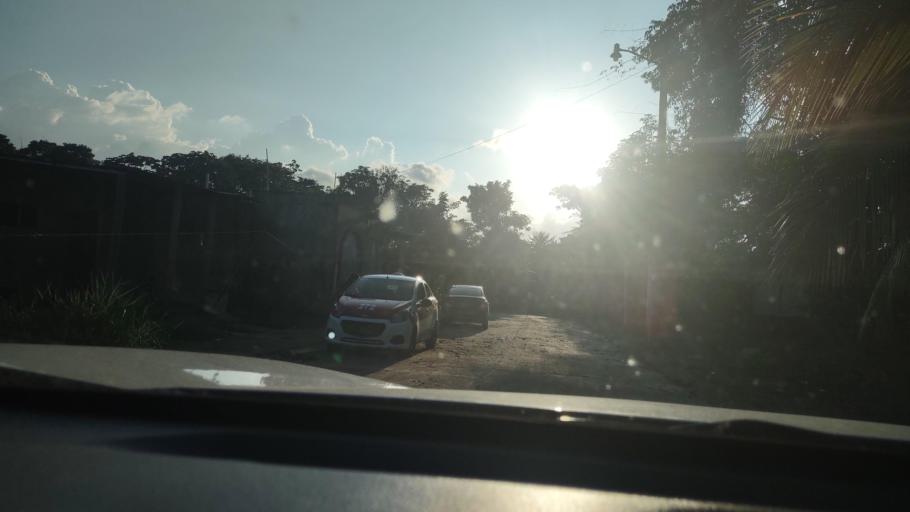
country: MX
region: Veracruz
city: Las Choapas
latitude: 17.9345
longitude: -94.1174
